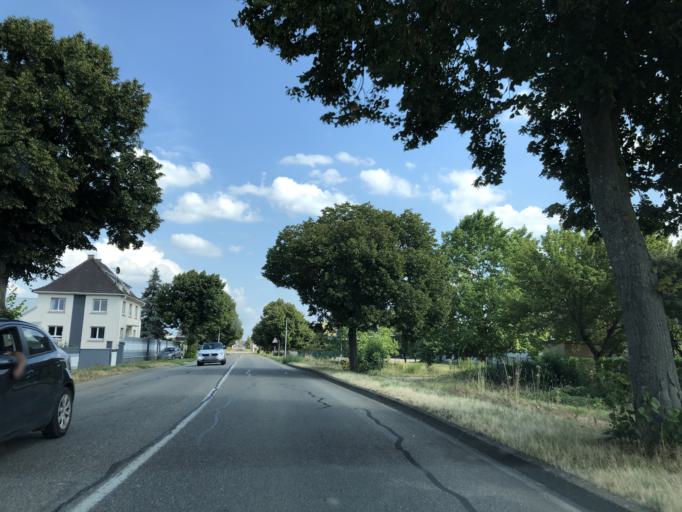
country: FR
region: Alsace
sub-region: Departement du Bas-Rhin
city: Erstein
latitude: 48.4251
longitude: 7.6323
